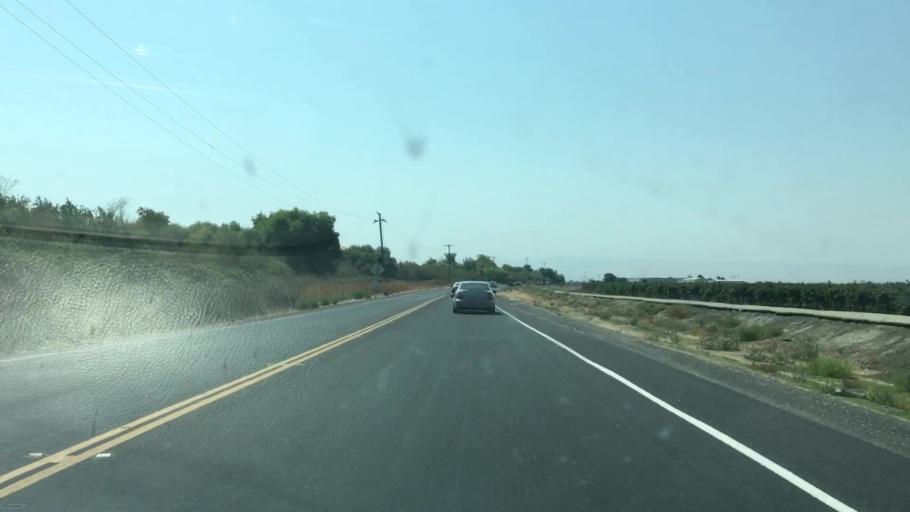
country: US
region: California
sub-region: San Joaquin County
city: Tracy
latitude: 37.8501
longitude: -121.4499
